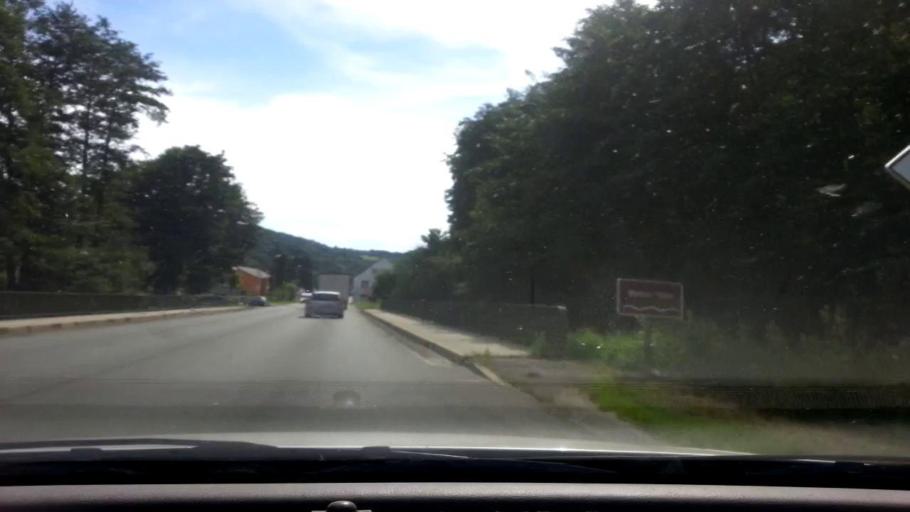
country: DE
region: Bavaria
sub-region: Upper Franconia
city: Bad Berneck im Fichtelgebirge
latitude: 50.0391
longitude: 11.6731
